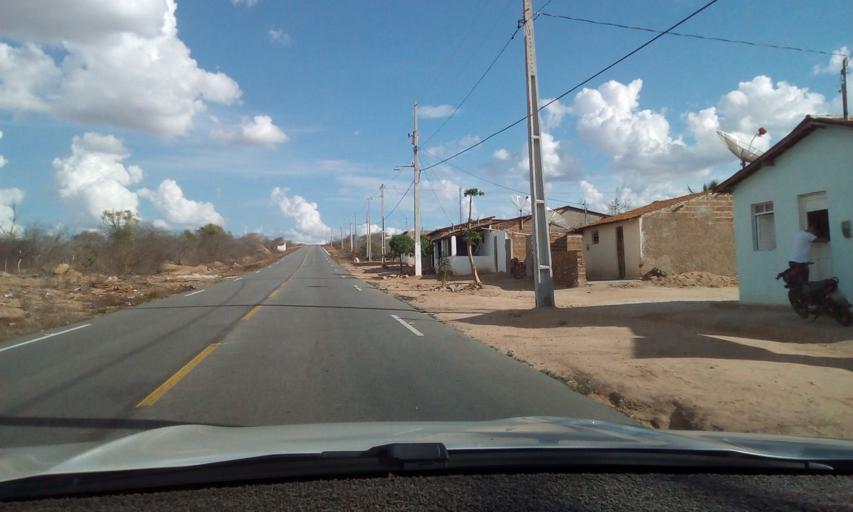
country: BR
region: Paraiba
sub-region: Soledade
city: Soledade
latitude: -6.8612
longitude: -36.4055
